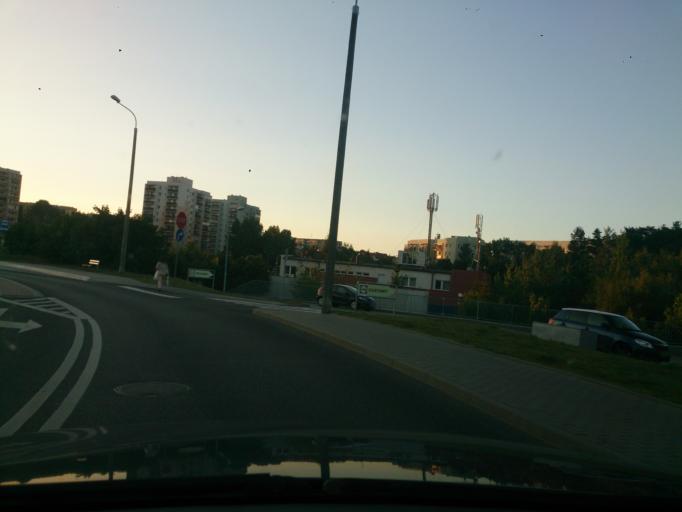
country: PL
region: Pomeranian Voivodeship
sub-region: Gdynia
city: Wielki Kack
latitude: 54.4699
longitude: 18.4916
